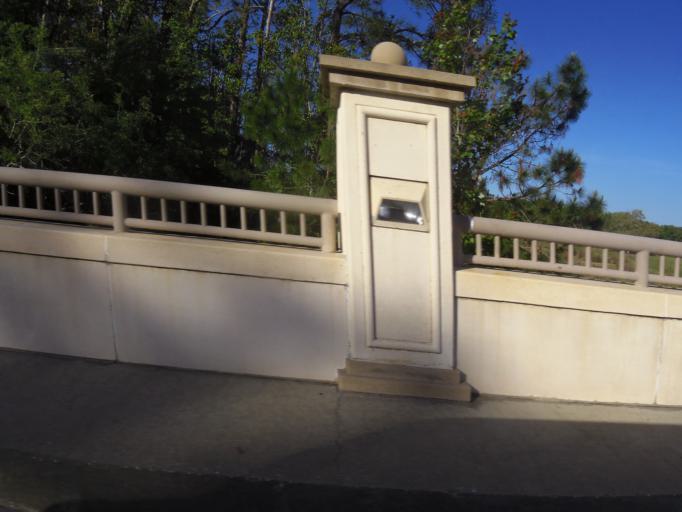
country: US
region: Florida
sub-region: Saint Johns County
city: Villano Beach
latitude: 29.9843
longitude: -81.4672
